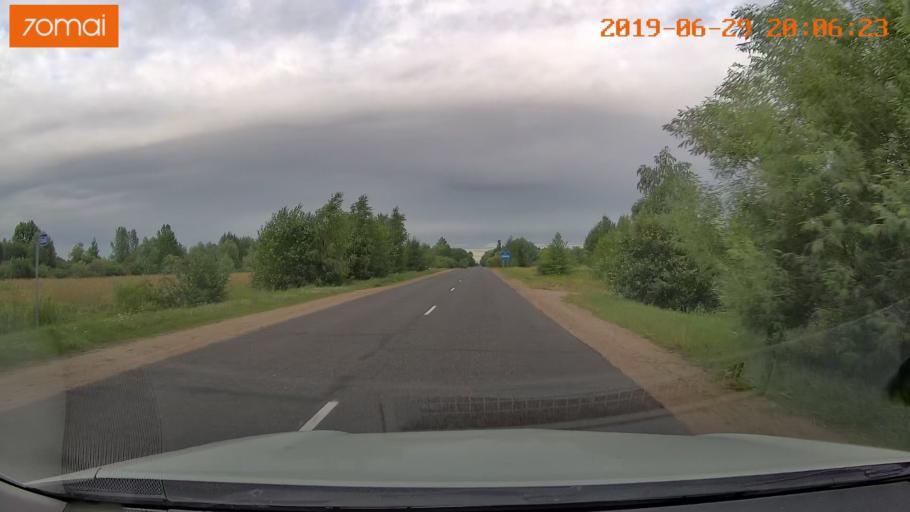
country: BY
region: Brest
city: Lahishyn
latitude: 52.3386
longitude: 26.0112
